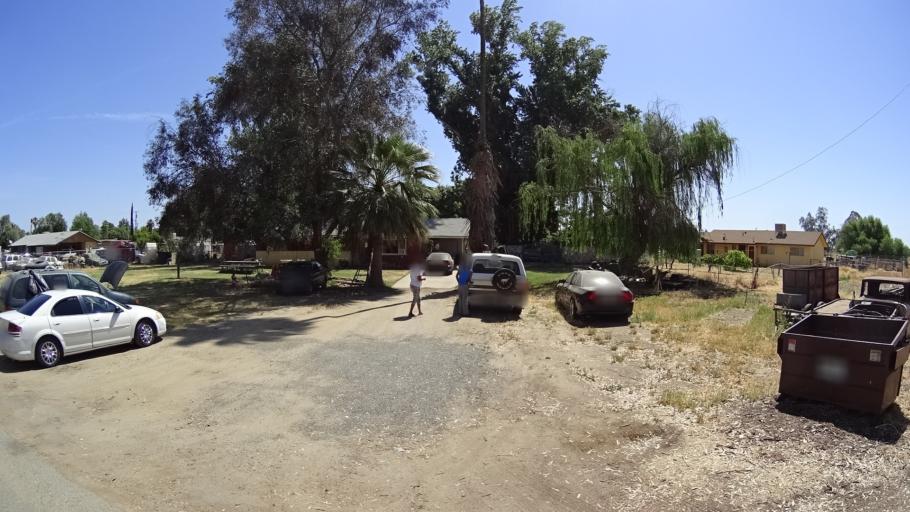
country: US
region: California
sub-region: Kings County
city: Lemoore
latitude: 36.2738
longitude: -119.7845
